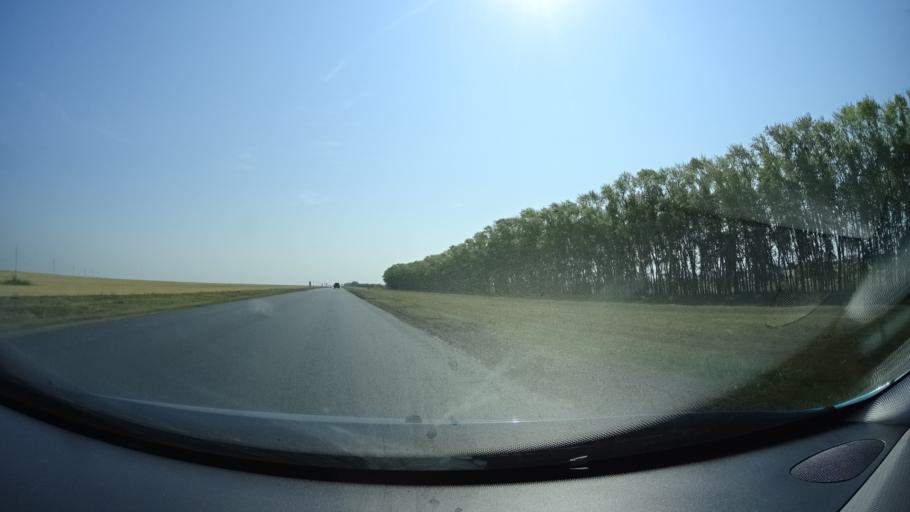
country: RU
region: Bashkortostan
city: Kabakovo
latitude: 54.4324
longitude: 56.0166
